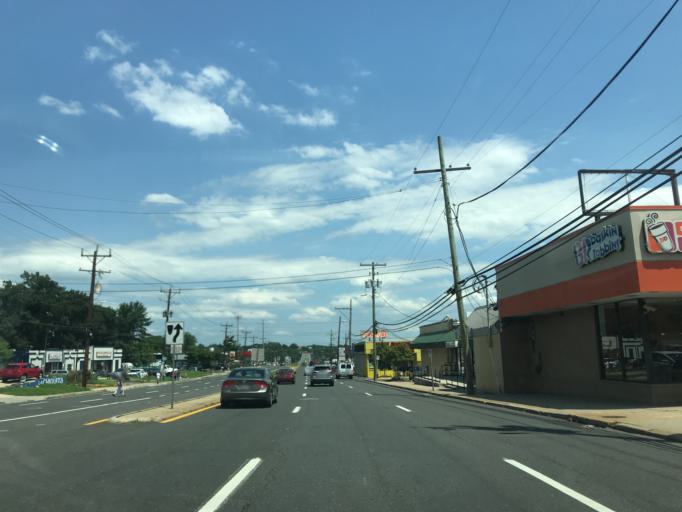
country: US
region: Maryland
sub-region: Prince George's County
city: Langley Park
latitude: 38.9835
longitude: -76.9776
